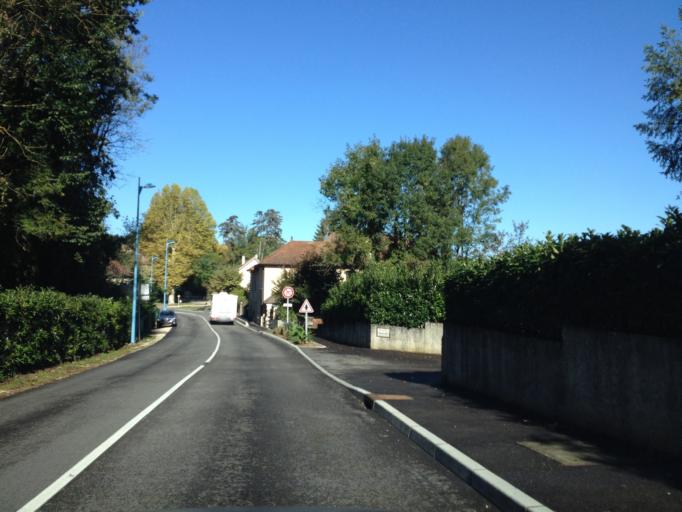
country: FR
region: Rhone-Alpes
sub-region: Departement de l'Isere
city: Curtin
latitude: 45.6512
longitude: 5.4697
